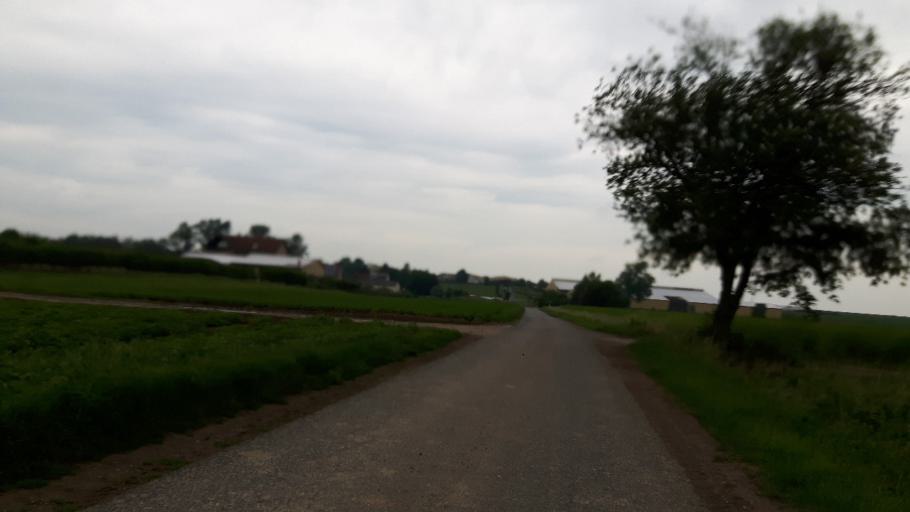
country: DE
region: Bavaria
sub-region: Regierungsbezirk Unterfranken
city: Unterpleichfeld
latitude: 49.8656
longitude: 10.0533
